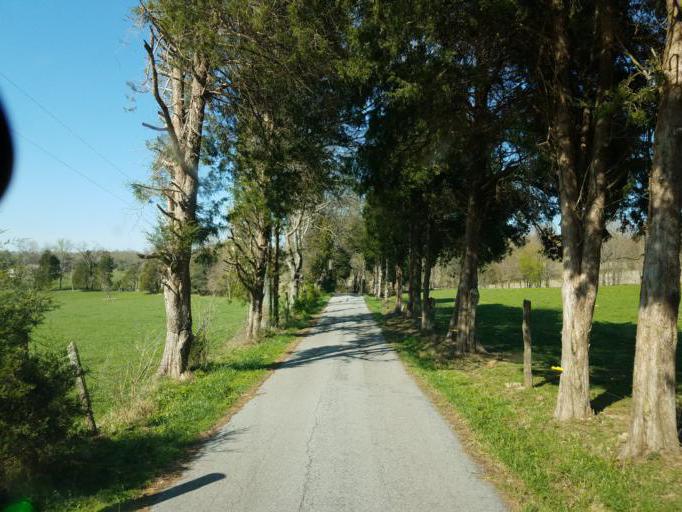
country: US
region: Kentucky
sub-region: Edmonson County
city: Brownsville
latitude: 37.1293
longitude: -86.1520
